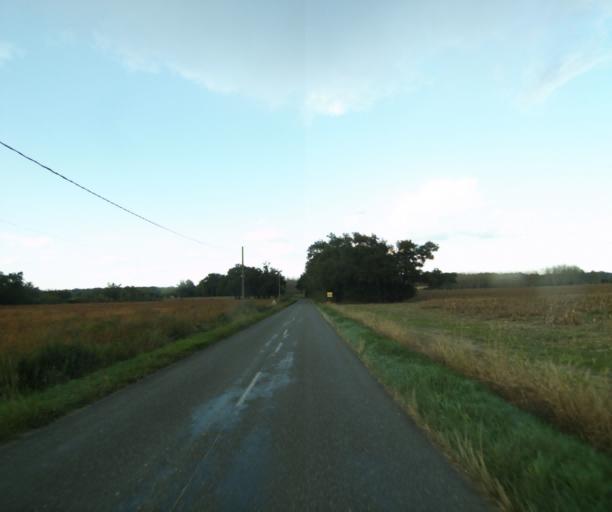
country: FR
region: Midi-Pyrenees
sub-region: Departement du Gers
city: Cazaubon
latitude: 43.9219
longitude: -0.0772
